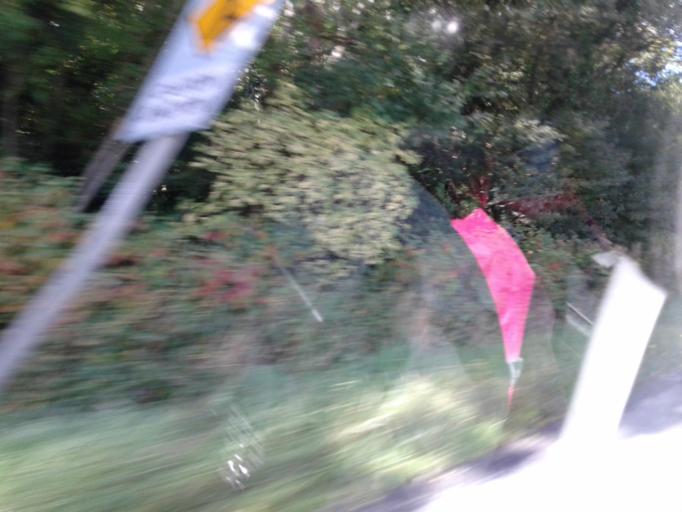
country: IE
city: Kentstown
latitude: 53.6382
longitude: -6.4964
